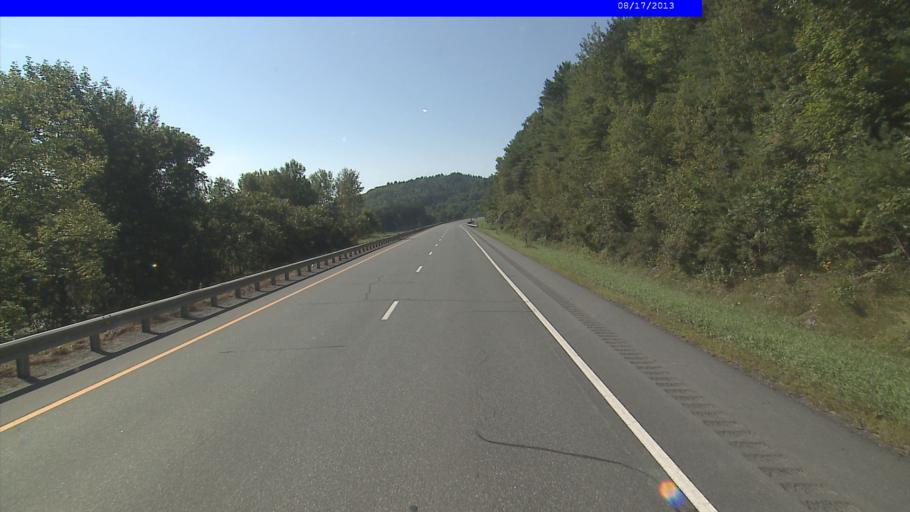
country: US
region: Vermont
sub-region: Windsor County
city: Windsor
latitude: 43.5134
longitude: -72.4074
